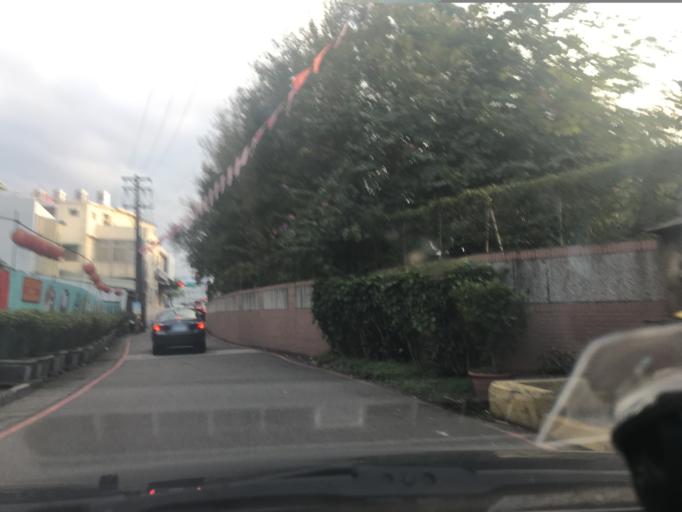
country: TW
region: Taiwan
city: Taoyuan City
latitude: 24.9649
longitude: 121.2350
